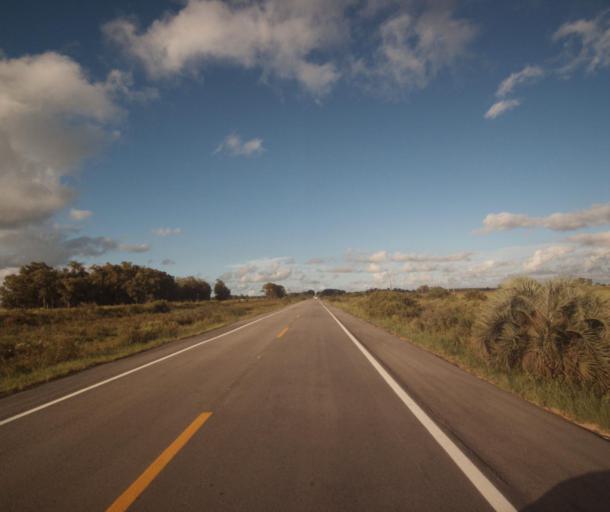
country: BR
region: Rio Grande do Sul
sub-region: Rio Grande
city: Rio Grande
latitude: -32.1337
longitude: -52.3733
